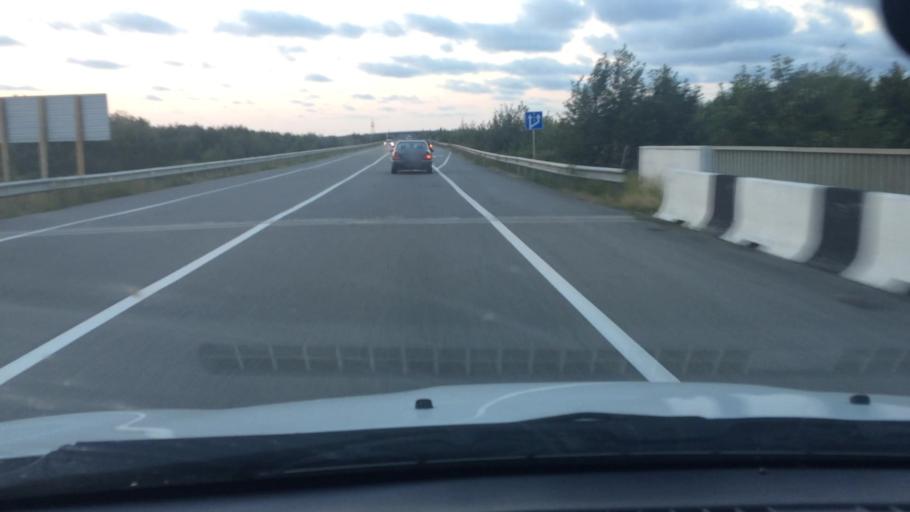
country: GE
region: Ajaria
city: Ochkhamuri
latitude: 41.8932
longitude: 41.8040
